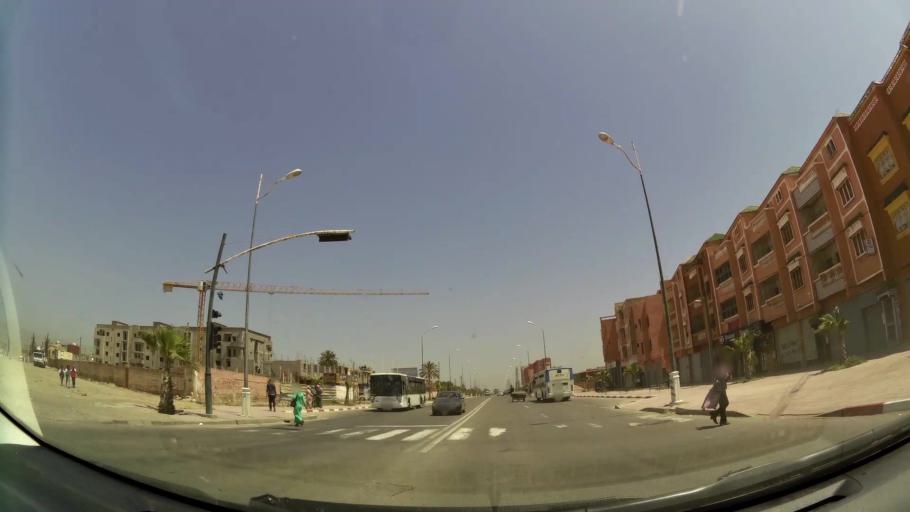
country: MA
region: Souss-Massa-Draa
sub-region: Inezgane-Ait Mellou
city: Inezgane
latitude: 30.3518
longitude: -9.4929
